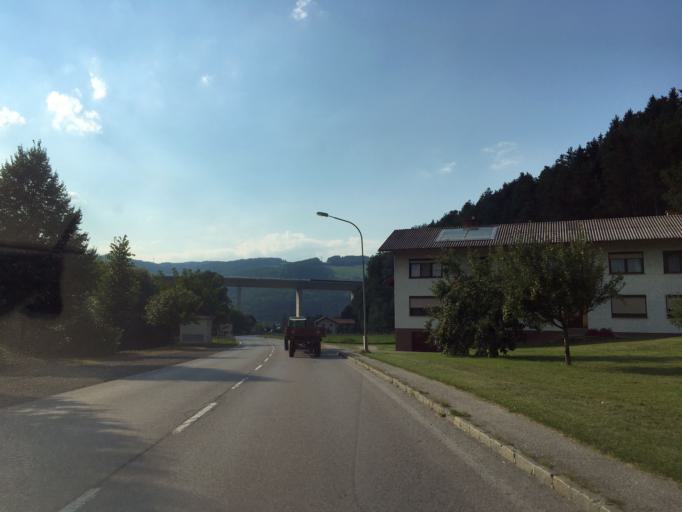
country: AT
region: Lower Austria
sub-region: Politischer Bezirk Neunkirchen
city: Grimmenstein
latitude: 47.6020
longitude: 16.1349
